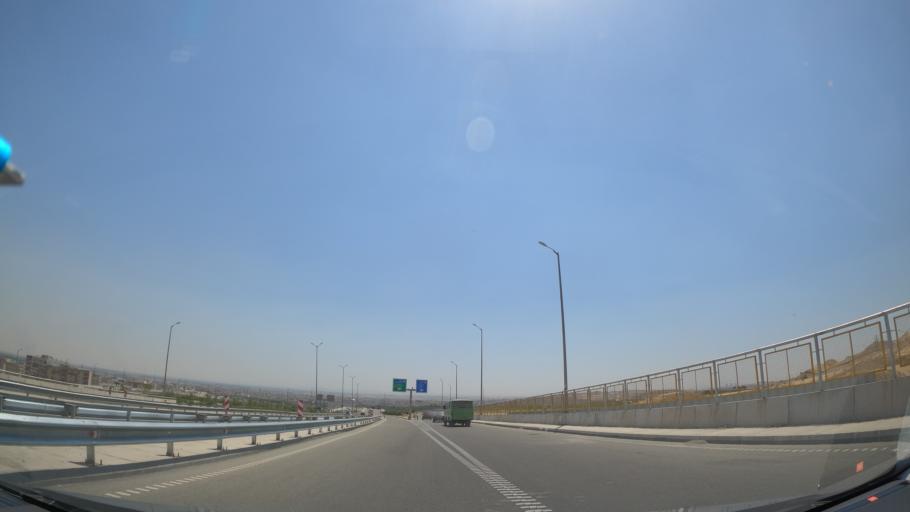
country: IR
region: Tehran
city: Shahr-e Qods
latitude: 35.7459
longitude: 51.1277
